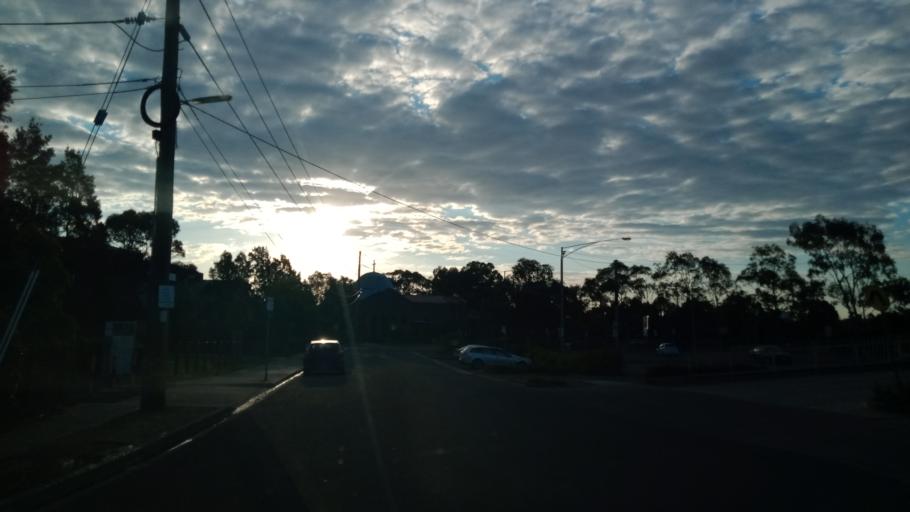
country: AU
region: Victoria
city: Glenferrie
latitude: -37.8297
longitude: 145.0523
